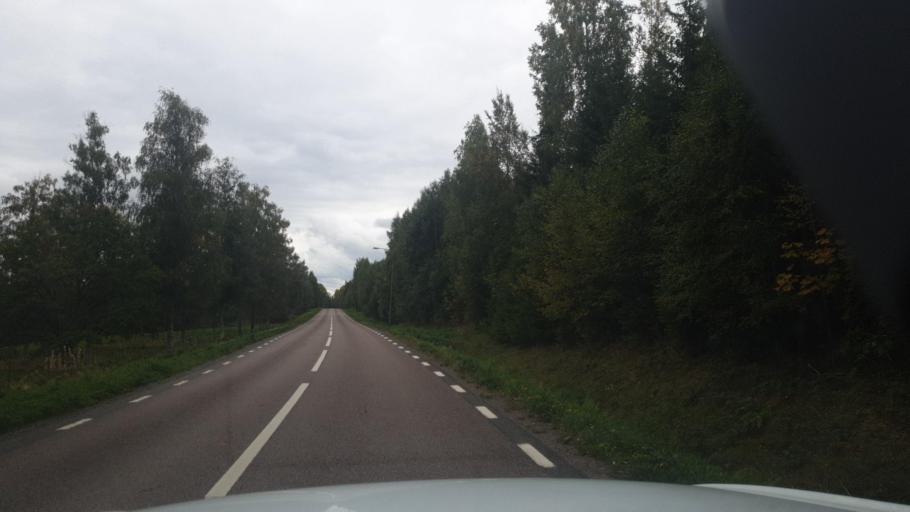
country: SE
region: Vaermland
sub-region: Sunne Kommun
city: Sunne
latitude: 59.8806
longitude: 12.9277
